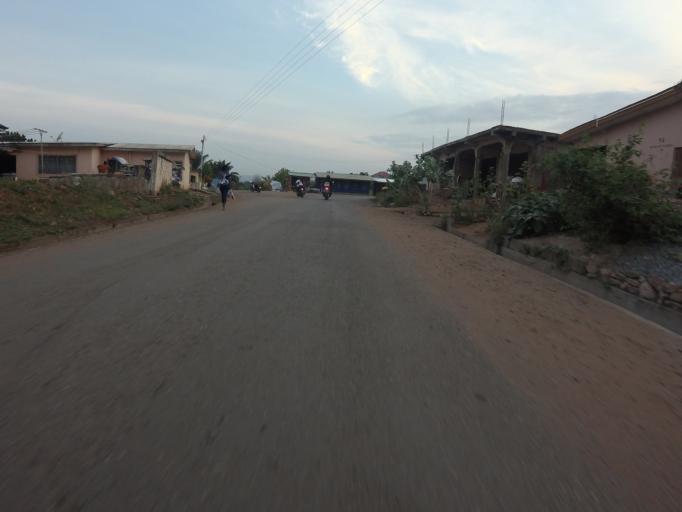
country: GH
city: Akropong
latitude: 6.1013
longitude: -0.0092
